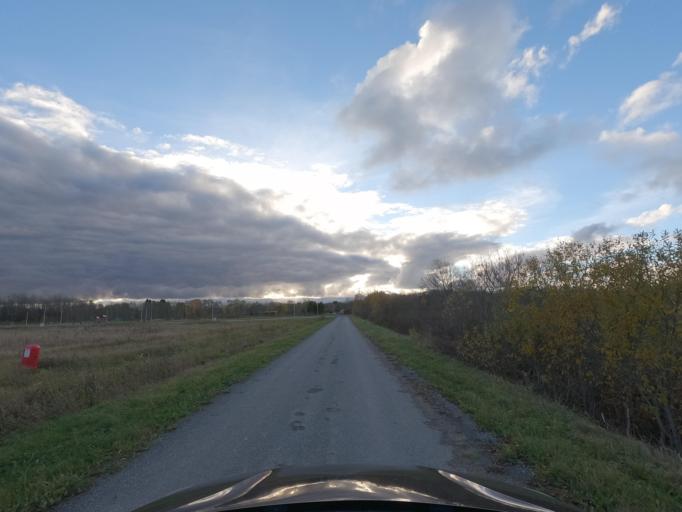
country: EE
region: Harju
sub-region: Saue vald
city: Laagri
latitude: 59.3677
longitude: 24.5679
